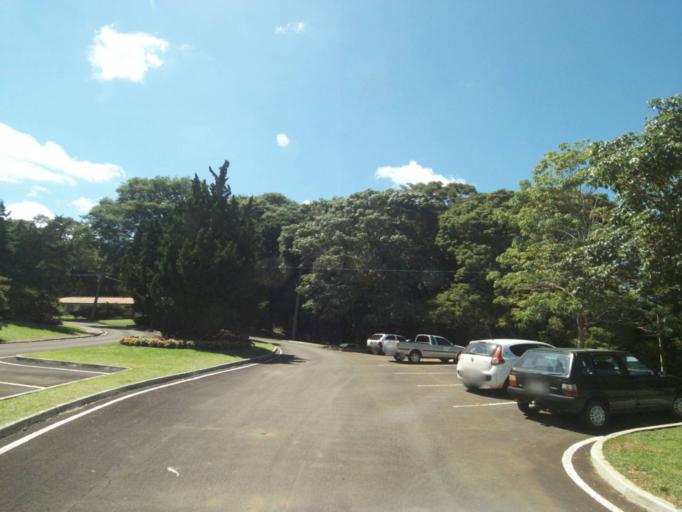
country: BR
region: Parana
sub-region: Chopinzinho
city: Chopinzinho
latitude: -25.7992
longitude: -52.1004
